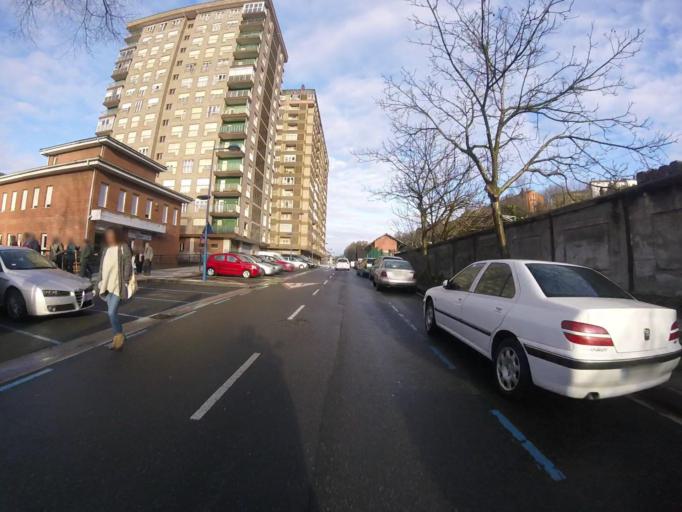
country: ES
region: Basque Country
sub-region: Provincia de Guipuzcoa
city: Errenteria
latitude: 43.3148
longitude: -1.8980
